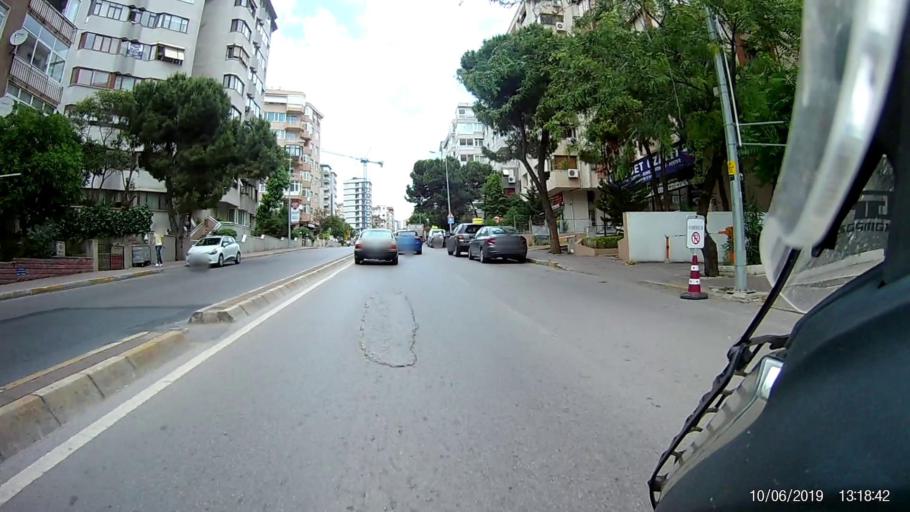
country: TR
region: Istanbul
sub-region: Atasehir
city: Atasehir
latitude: 40.9589
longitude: 29.1018
